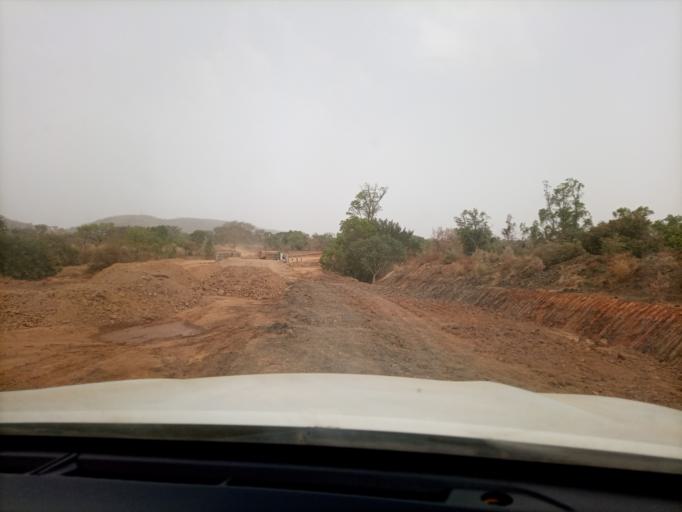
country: ET
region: Oromiya
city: Mendi
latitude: 10.2054
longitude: 35.0886
